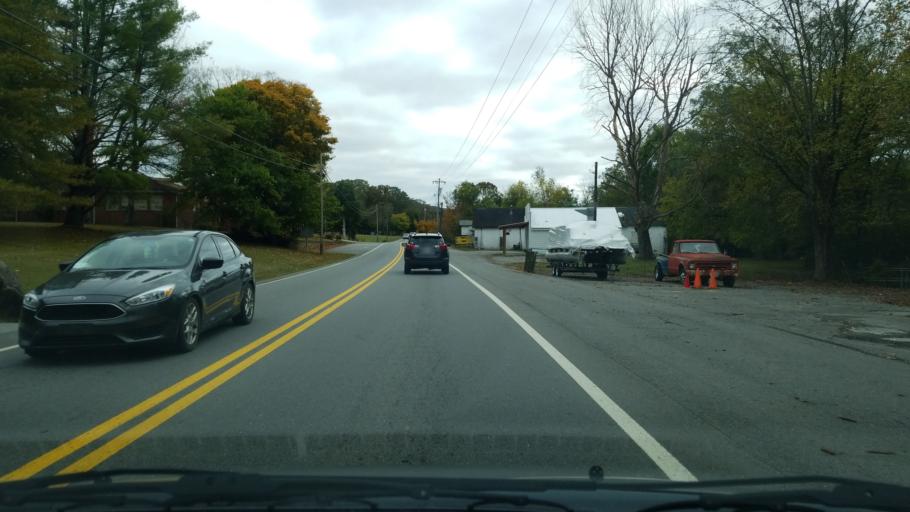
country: US
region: Tennessee
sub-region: Hamilton County
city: Sale Creek
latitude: 35.3594
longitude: -84.9930
